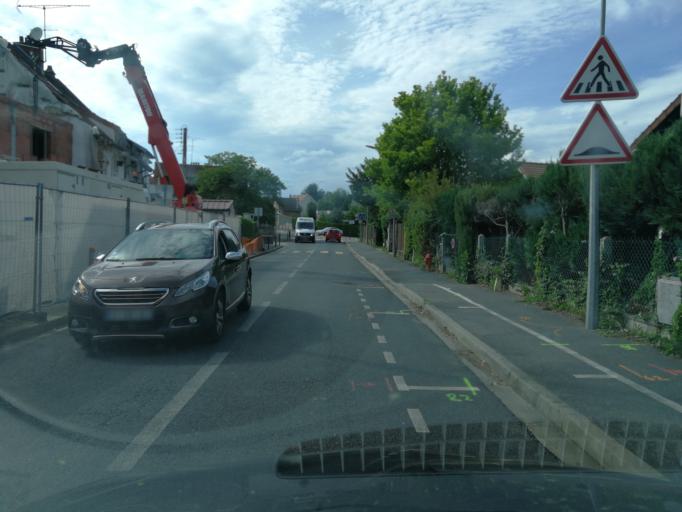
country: FR
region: Ile-de-France
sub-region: Departement des Yvelines
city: Saint-Remy-les-Chevreuse
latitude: 48.6990
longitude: 2.1014
